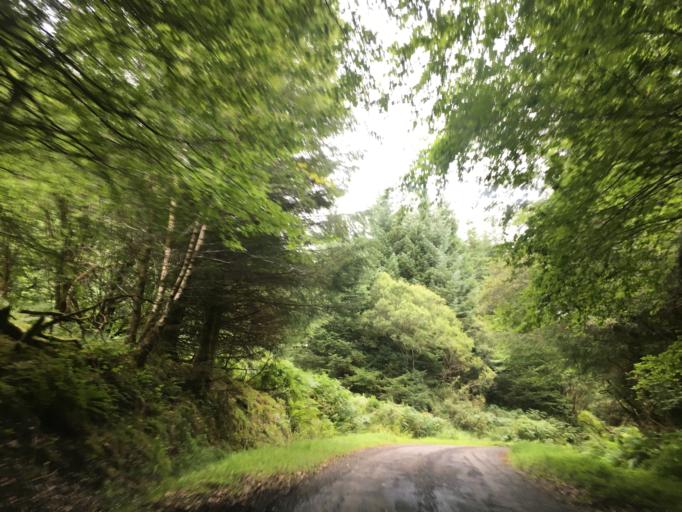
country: GB
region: Scotland
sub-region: Argyll and Bute
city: Oban
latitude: 56.2848
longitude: -5.3007
